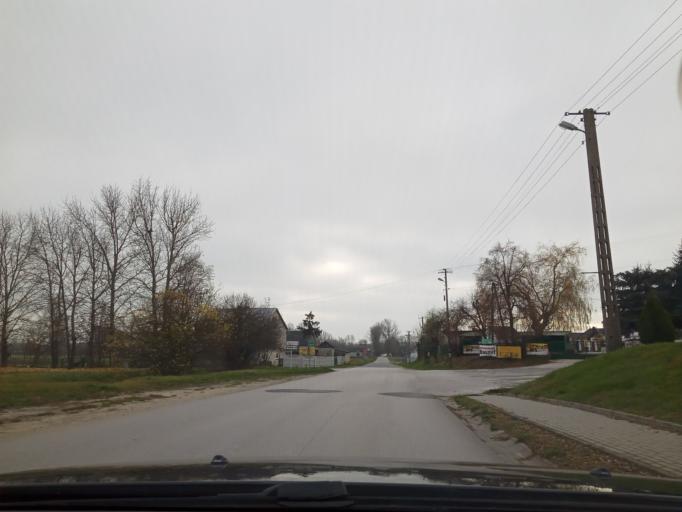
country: PL
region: Swietokrzyskie
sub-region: Powiat jedrzejowski
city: Imielno
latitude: 50.5839
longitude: 20.4497
